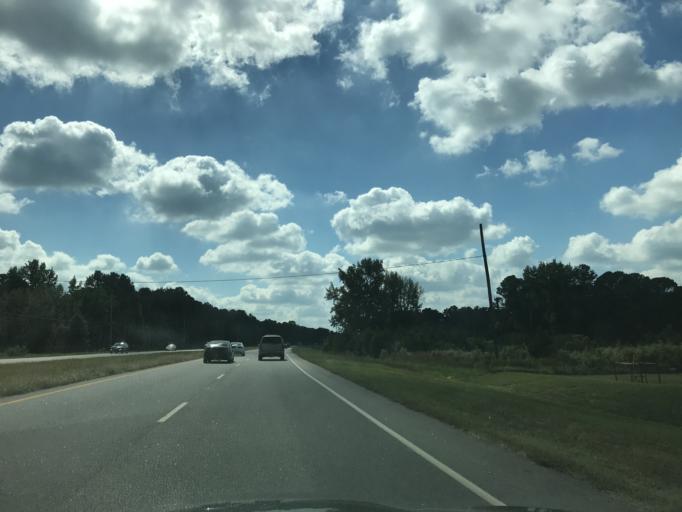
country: US
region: North Carolina
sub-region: Wake County
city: Wake Forest
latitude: 35.9982
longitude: -78.5244
